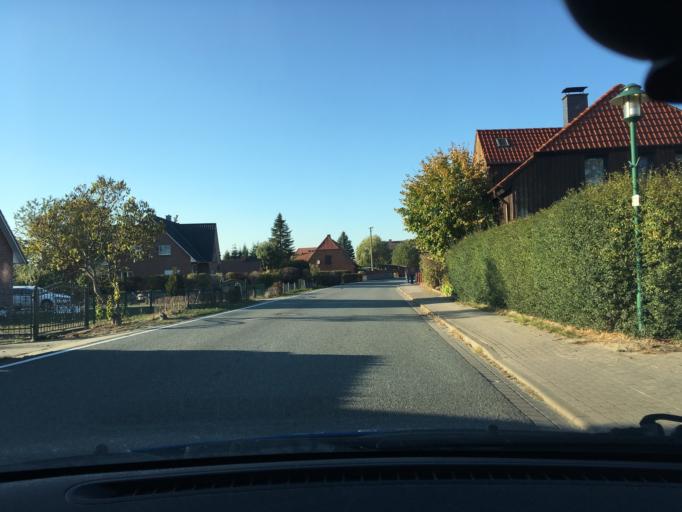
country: DE
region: Lower Saxony
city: Neu Darchau
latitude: 53.2791
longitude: 10.9337
